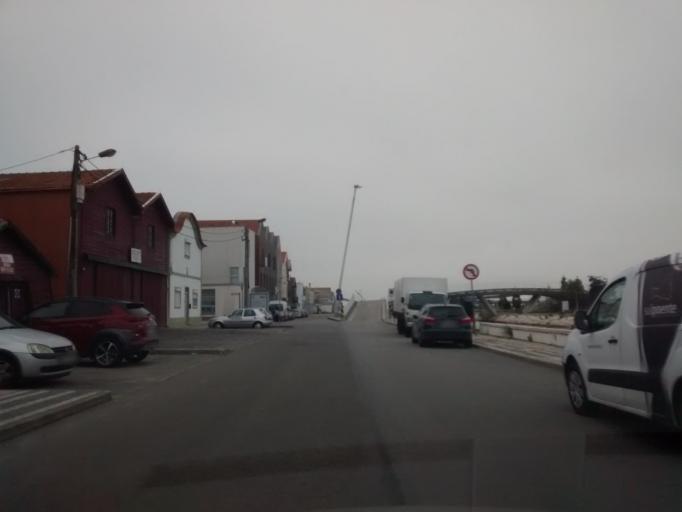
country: PT
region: Aveiro
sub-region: Aveiro
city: Aveiro
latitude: 40.6470
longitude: -8.6513
